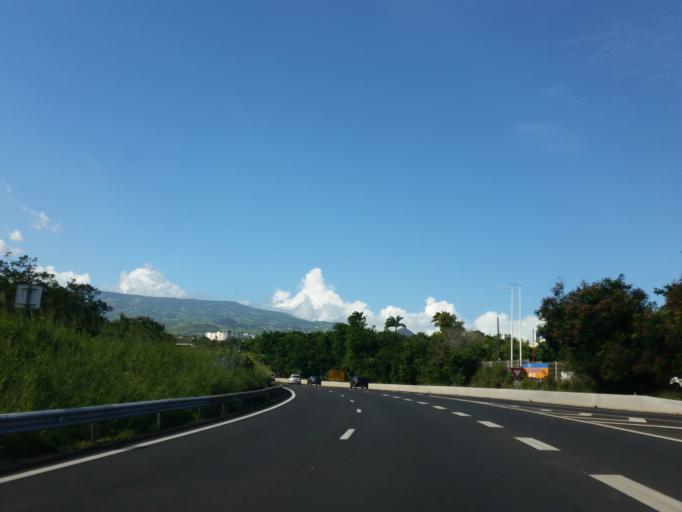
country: RE
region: Reunion
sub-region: Reunion
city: Saint-Pierre
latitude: -21.3332
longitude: 55.4613
